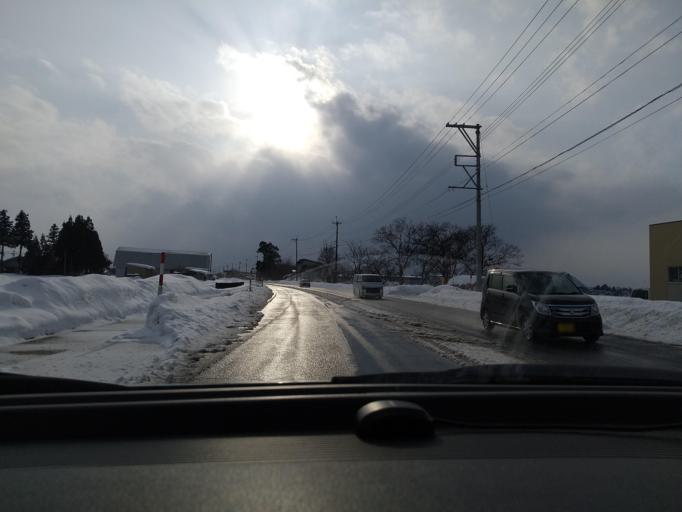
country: JP
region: Akita
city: Omagari
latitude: 39.5036
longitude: 140.5053
